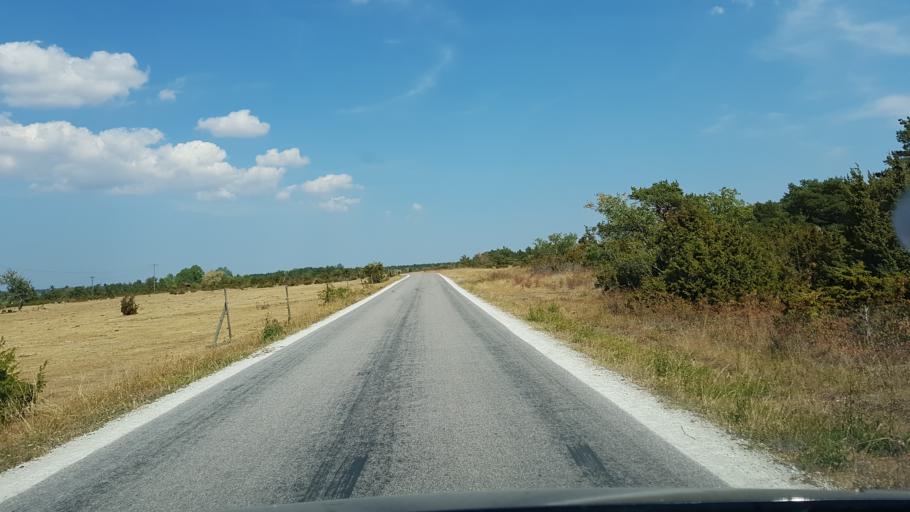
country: SE
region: Gotland
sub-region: Gotland
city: Visby
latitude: 57.6604
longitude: 18.3724
